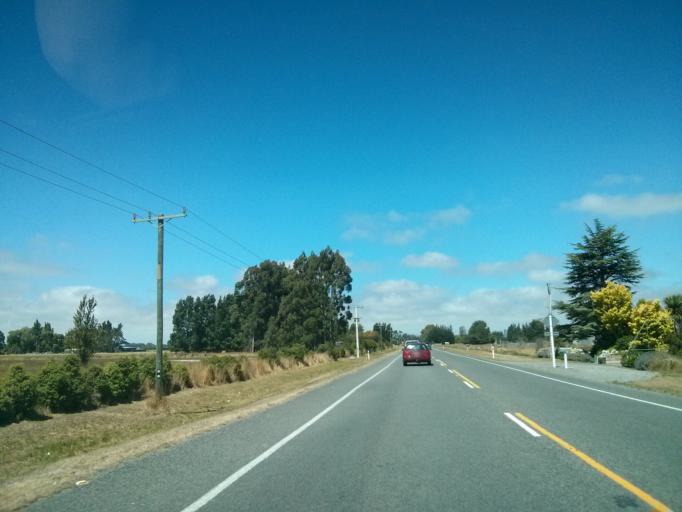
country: NZ
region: Canterbury
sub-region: Waimakariri District
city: Kaiapoi
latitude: -43.3932
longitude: 172.5924
